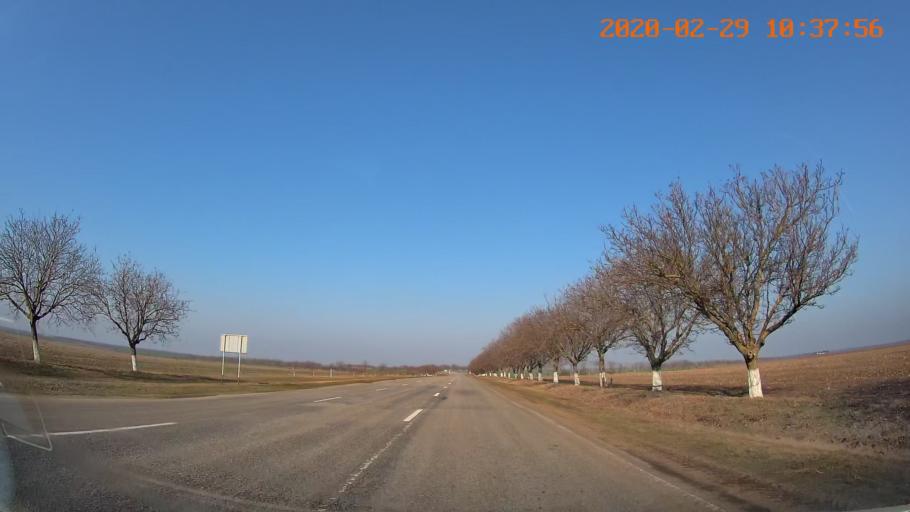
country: MD
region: Anenii Noi
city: Varnita
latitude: 47.0114
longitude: 29.4817
